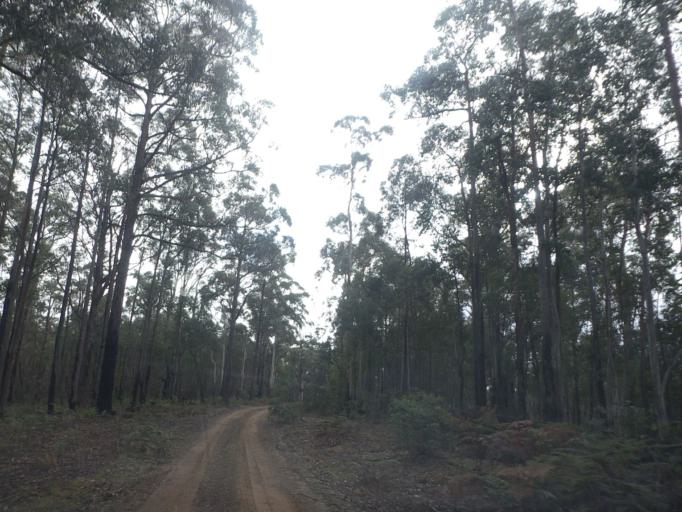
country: AU
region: Victoria
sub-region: Moorabool
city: Bacchus Marsh
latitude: -37.4468
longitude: 144.3253
